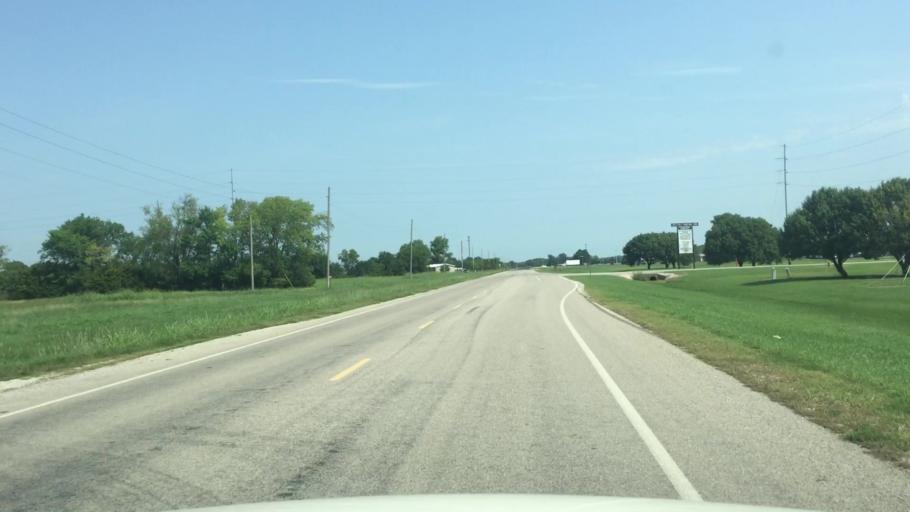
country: US
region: Kansas
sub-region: Montgomery County
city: Coffeyville
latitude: 37.0937
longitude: -95.5861
